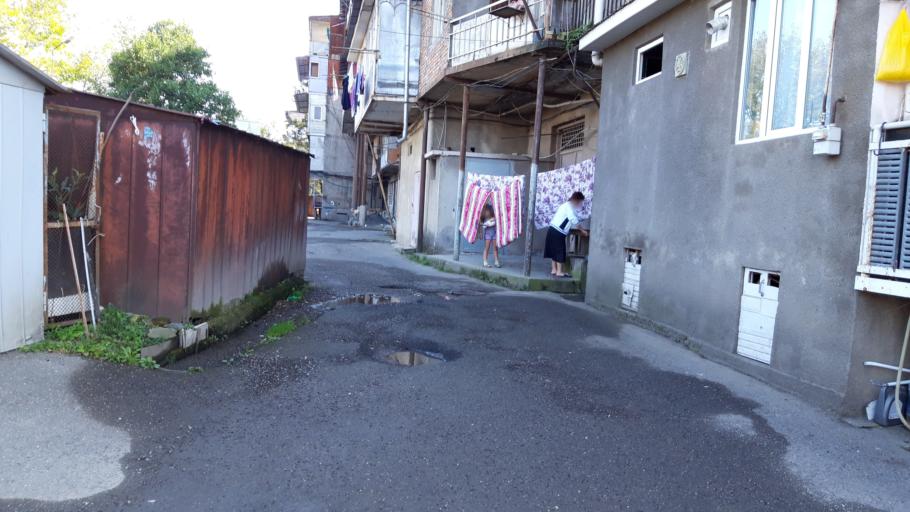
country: GE
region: Imereti
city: Samtredia
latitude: 42.1607
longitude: 42.3379
